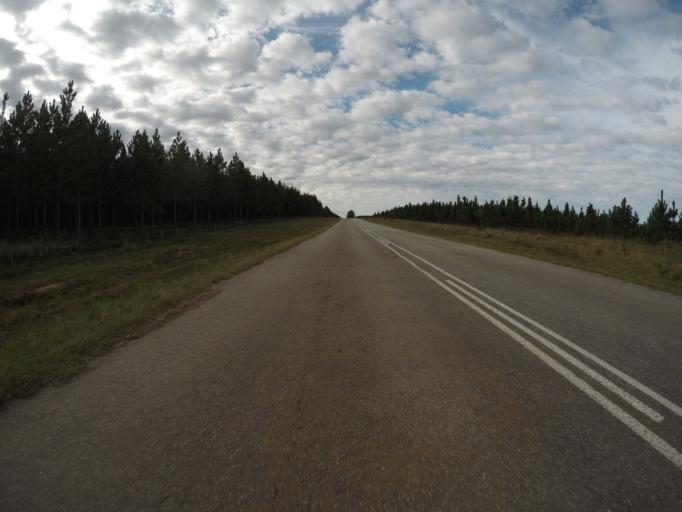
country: ZA
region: Eastern Cape
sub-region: Cacadu District Municipality
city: Kareedouw
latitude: -34.0261
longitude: 24.3694
